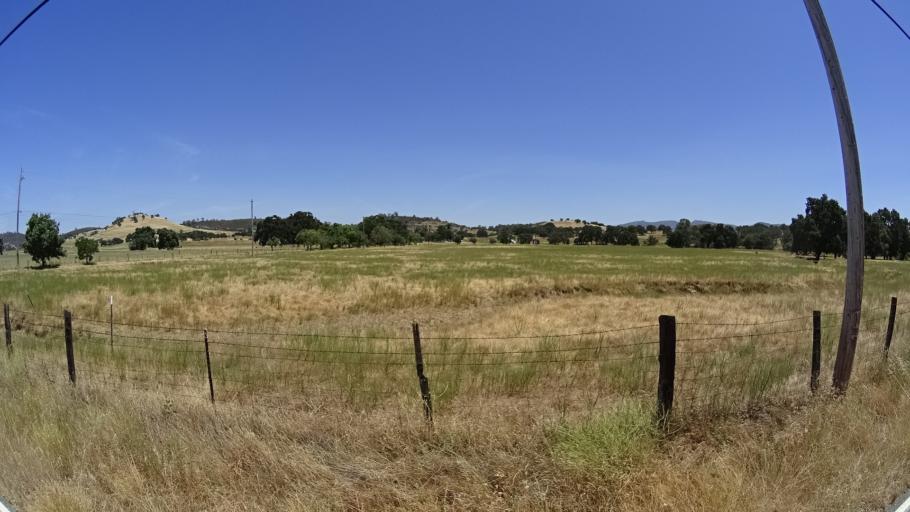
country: US
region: California
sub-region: Calaveras County
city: Valley Springs
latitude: 38.2128
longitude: -120.8252
